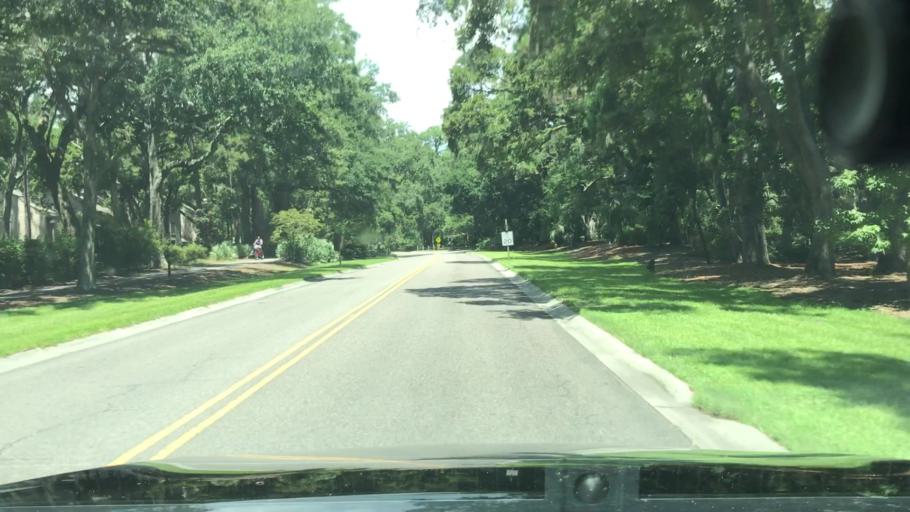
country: US
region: South Carolina
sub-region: Beaufort County
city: Hilton Head Island
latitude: 32.1362
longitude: -80.8050
